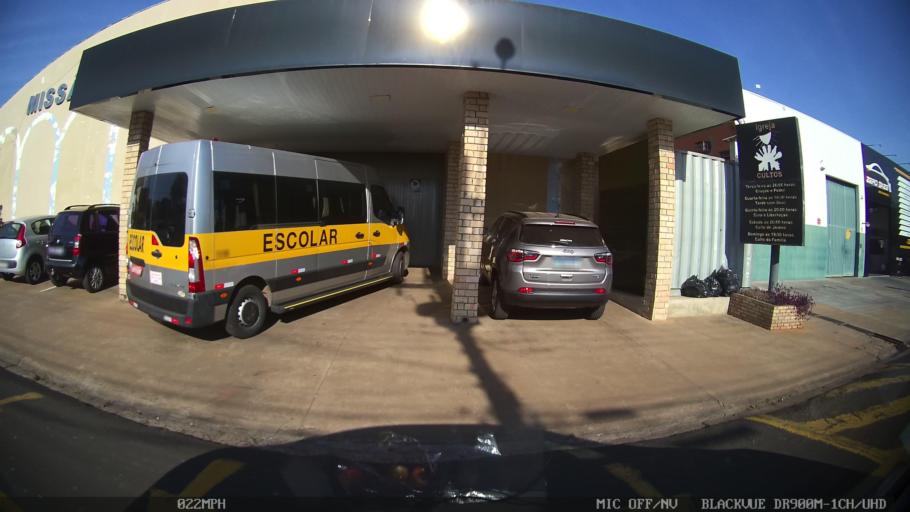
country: BR
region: Sao Paulo
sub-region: Sao Jose Do Rio Preto
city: Sao Jose do Rio Preto
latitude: -20.7923
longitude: -49.3620
